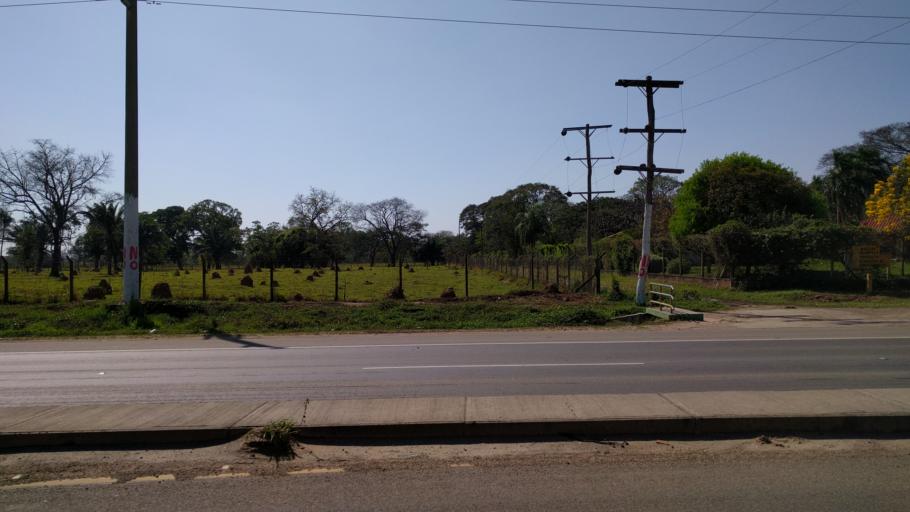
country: BO
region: Santa Cruz
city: Cotoca
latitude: -17.7655
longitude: -63.0412
